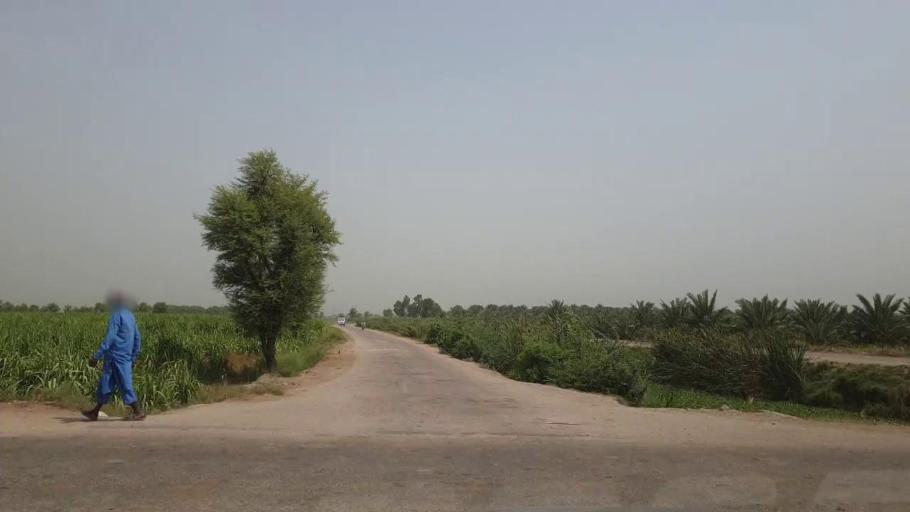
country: PK
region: Sindh
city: Gambat
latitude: 27.4009
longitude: 68.5516
